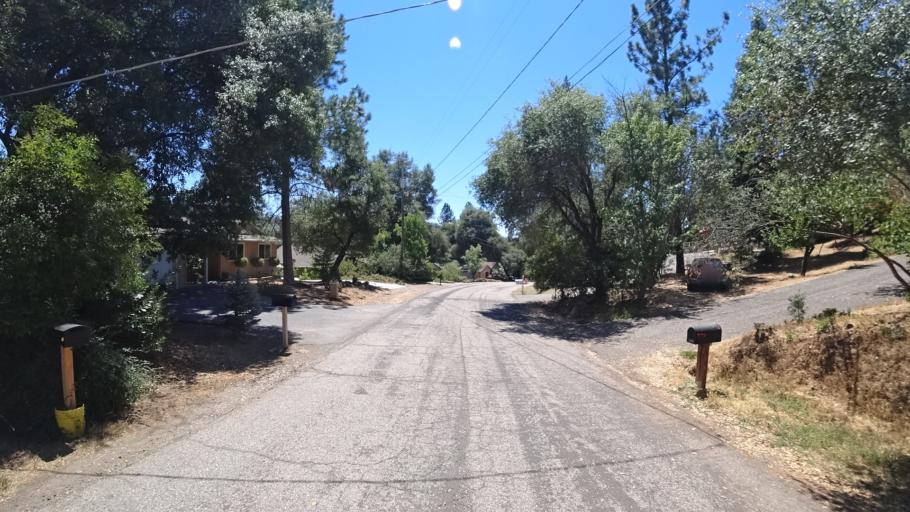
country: US
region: California
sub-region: Calaveras County
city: Murphys
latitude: 38.1347
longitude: -120.4365
